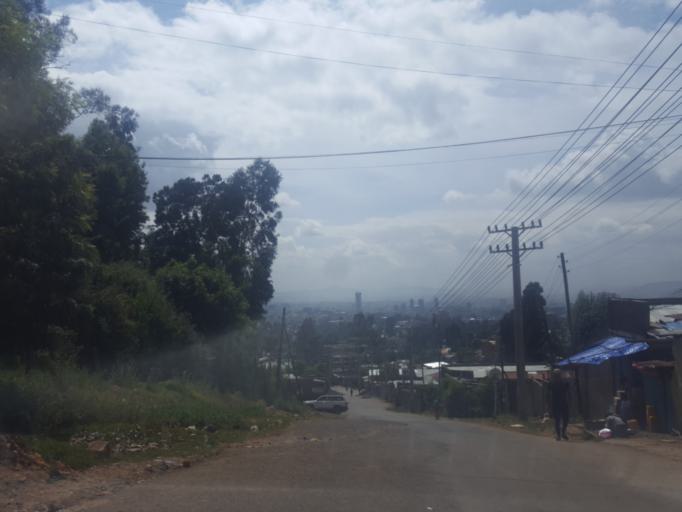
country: ET
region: Adis Abeba
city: Addis Ababa
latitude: 9.0662
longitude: 38.7417
